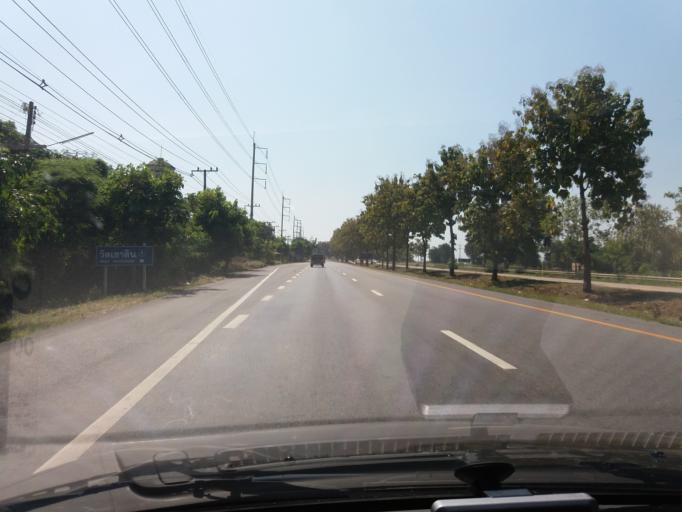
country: TH
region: Chai Nat
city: Sankhaburi
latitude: 15.1102
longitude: 100.1415
